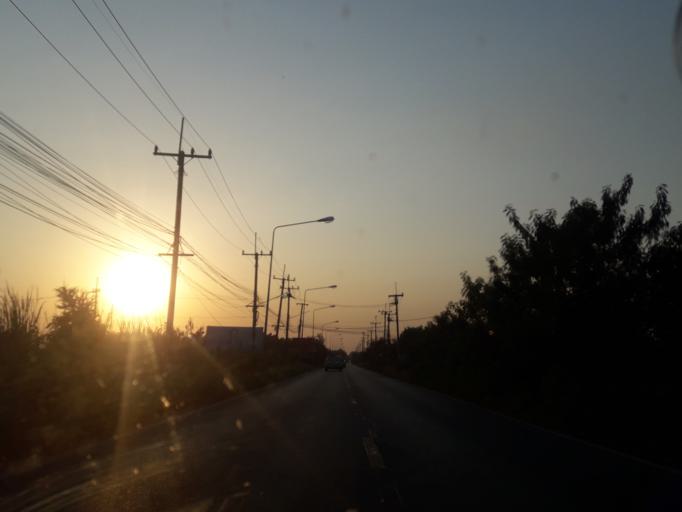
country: TH
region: Pathum Thani
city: Nong Suea
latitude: 14.1314
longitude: 100.7907
